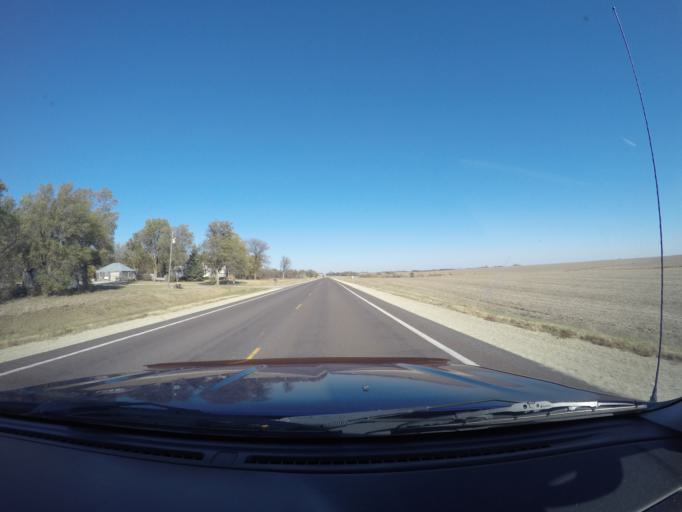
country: US
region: Kansas
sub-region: Marshall County
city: Blue Rapids
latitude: 39.6140
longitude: -96.7497
